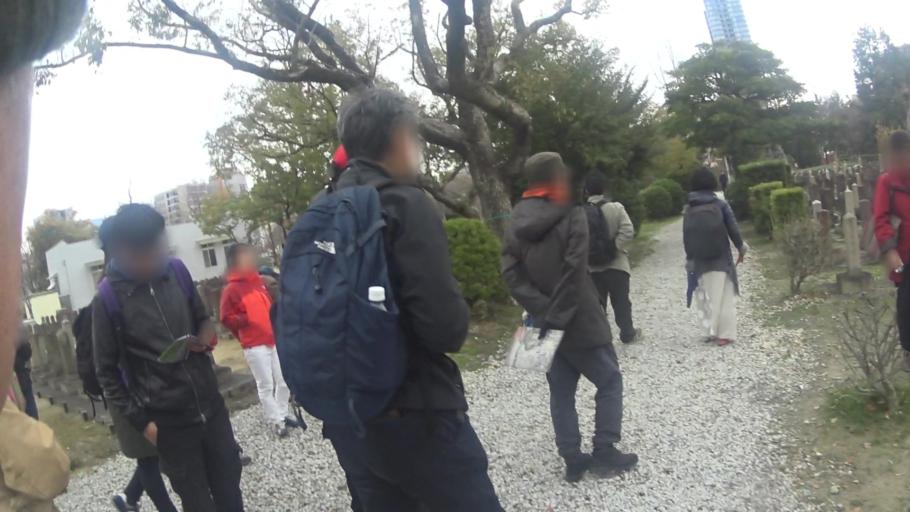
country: JP
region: Osaka
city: Osaka-shi
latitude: 34.6725
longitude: 135.5284
